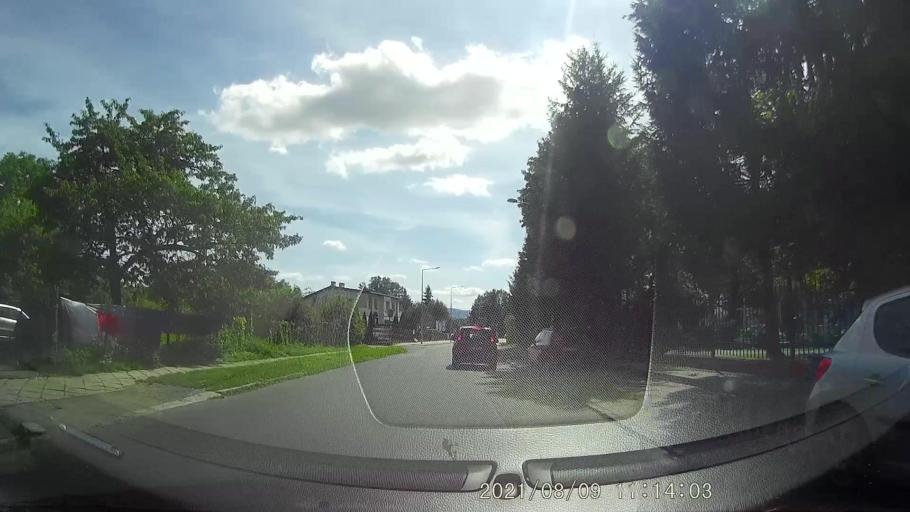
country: PL
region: Lower Silesian Voivodeship
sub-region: Powiat klodzki
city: Klodzko
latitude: 50.4405
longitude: 16.6415
